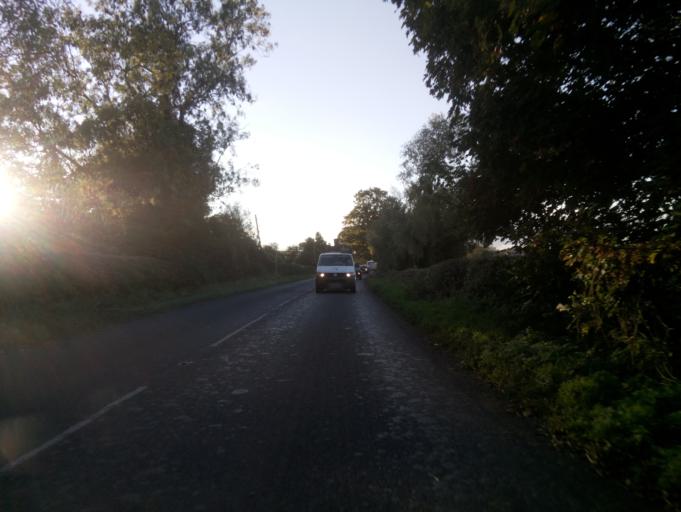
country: GB
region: England
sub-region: Gloucestershire
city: Tewkesbury
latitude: 52.0003
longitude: -2.1806
